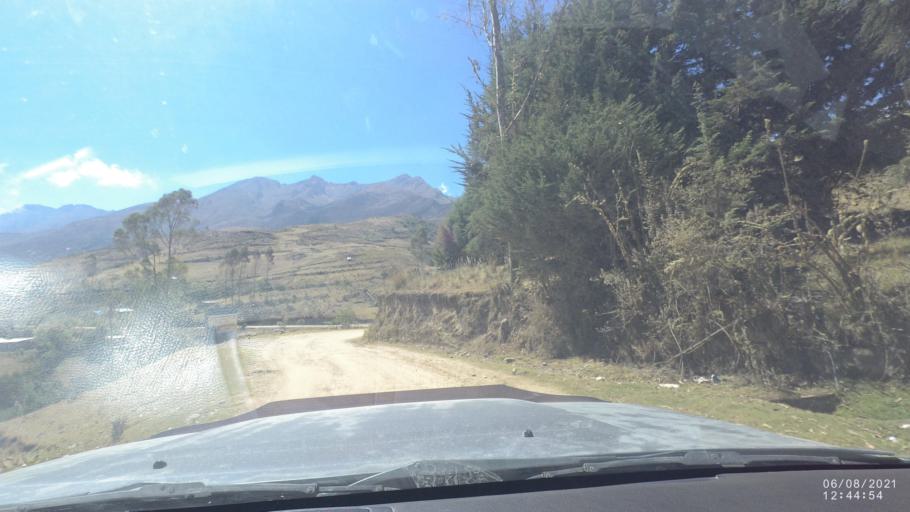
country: BO
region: Cochabamba
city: Colchani
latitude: -16.7670
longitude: -66.6644
